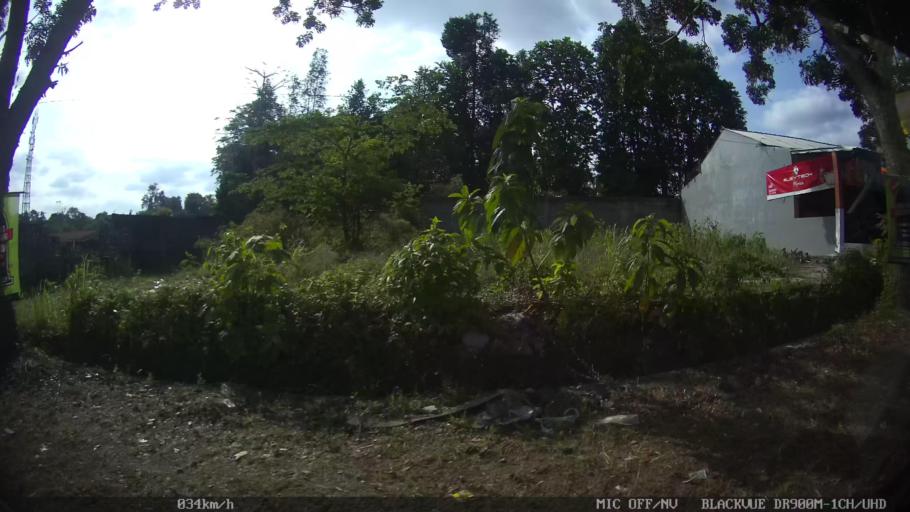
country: ID
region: Central Java
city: Candi Prambanan
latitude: -7.7313
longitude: 110.4620
